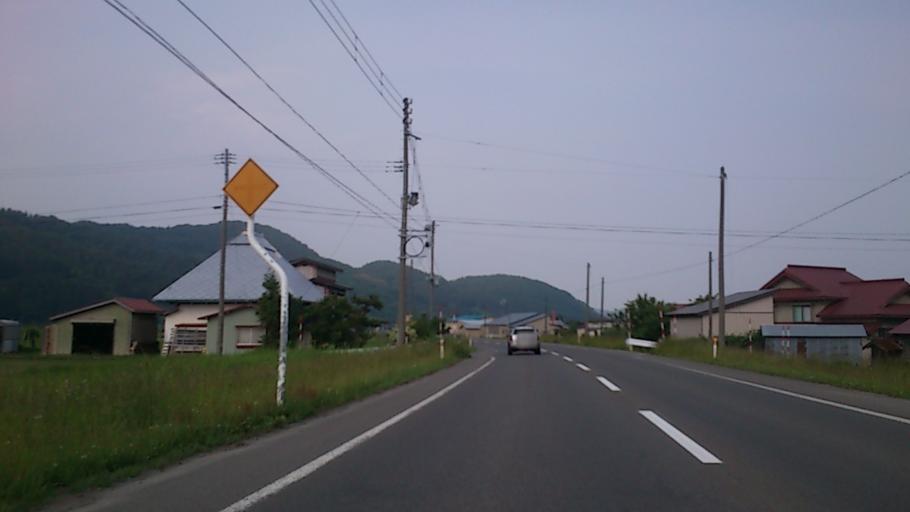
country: JP
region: Aomori
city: Hirosaki
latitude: 40.5844
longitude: 140.3087
